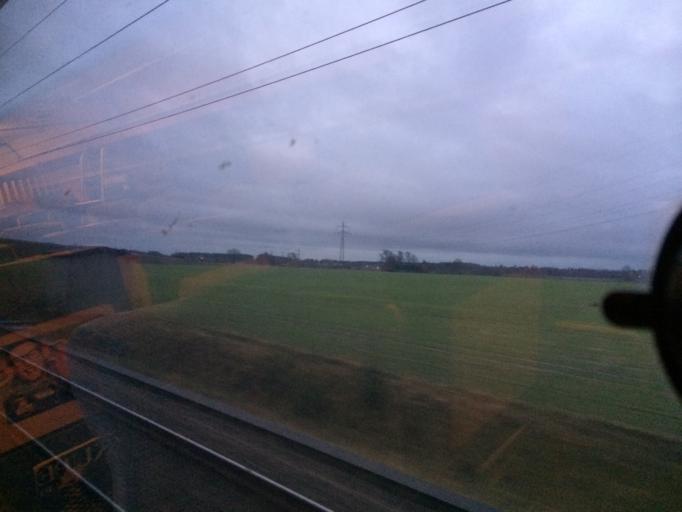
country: SE
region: Skane
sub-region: Kavlinge Kommun
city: Hofterup
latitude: 55.8317
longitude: 12.9901
